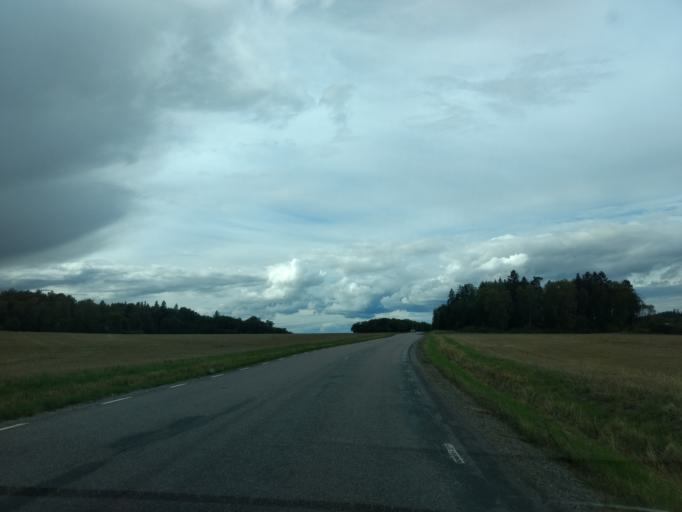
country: SE
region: Uppsala
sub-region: Habo Kommun
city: Balsta
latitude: 59.6677
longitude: 17.5499
